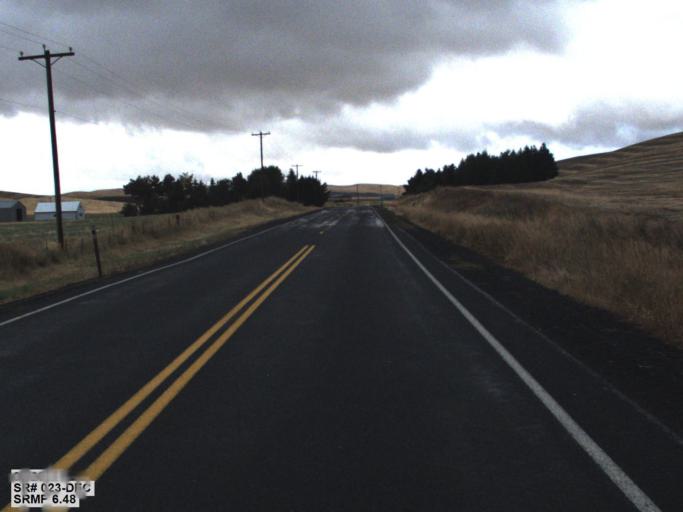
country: US
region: Washington
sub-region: Whitman County
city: Colfax
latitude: 47.0132
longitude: -117.4850
